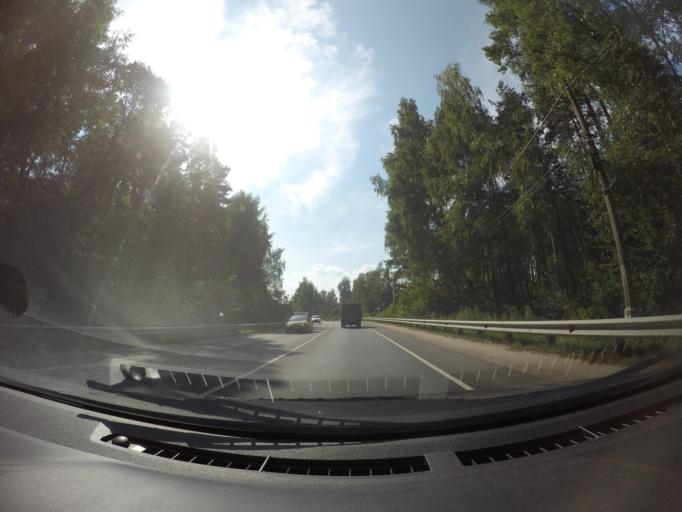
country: RU
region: Moskovskaya
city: Ramenskoye
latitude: 55.6368
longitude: 38.2929
